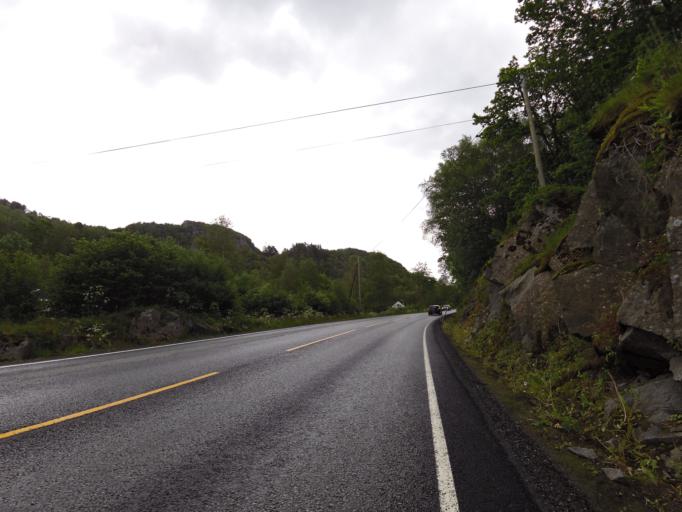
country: NO
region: Vest-Agder
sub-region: Farsund
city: Farsund
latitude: 58.1025
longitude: 6.8888
